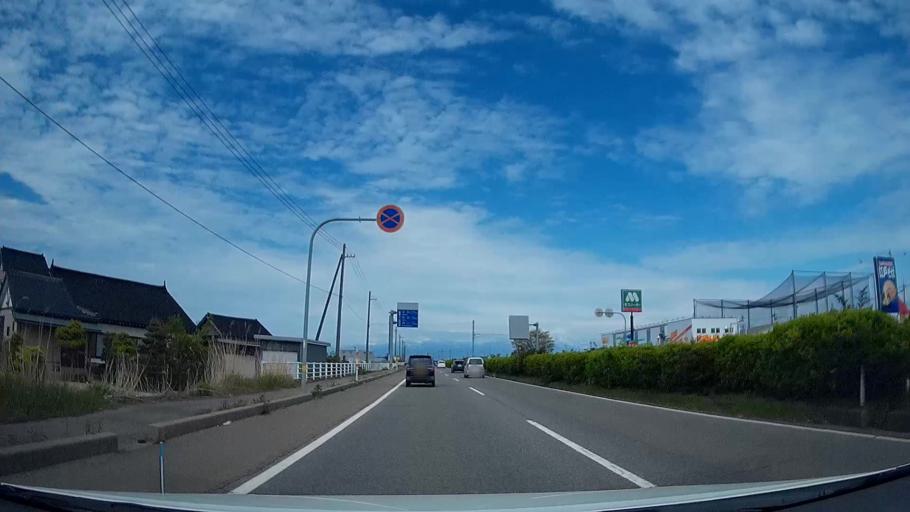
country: JP
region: Toyama
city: Kuragaki-kosugi
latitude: 36.7262
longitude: 137.1520
